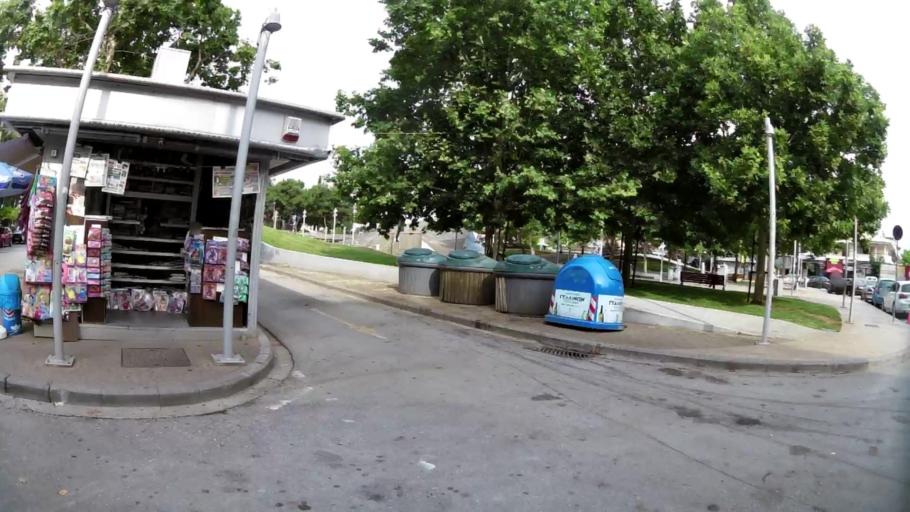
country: GR
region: Central Macedonia
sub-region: Nomos Thessalonikis
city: Thermi
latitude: 40.5470
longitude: 23.0202
